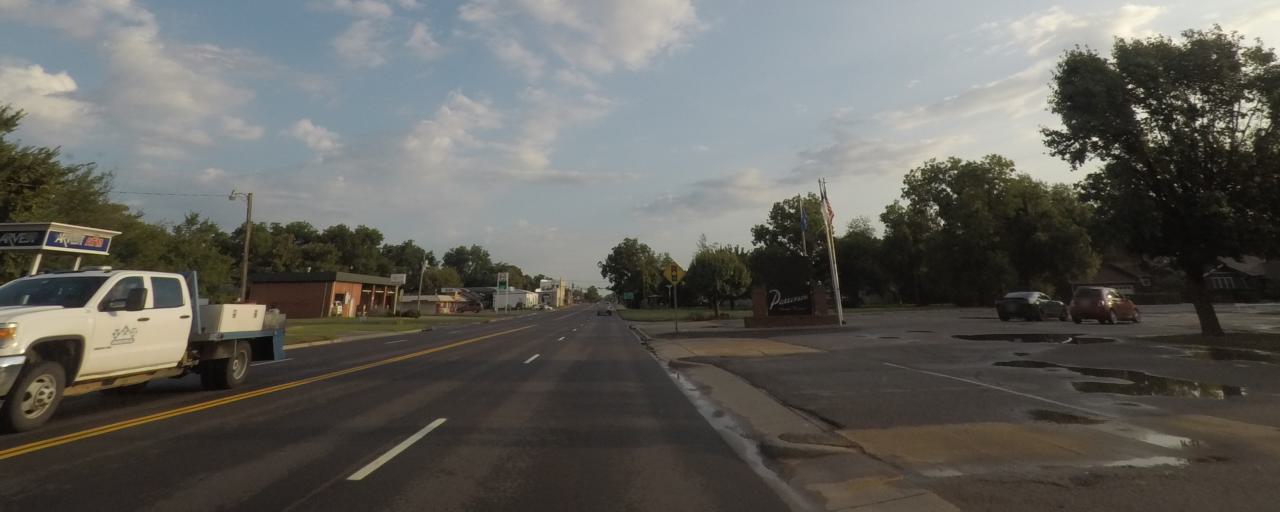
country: US
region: Oklahoma
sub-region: Stephens County
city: Comanche
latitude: 34.3662
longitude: -97.9642
